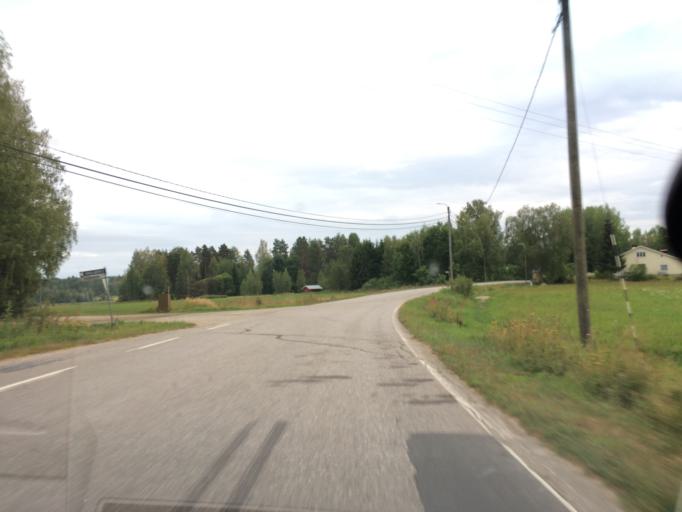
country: FI
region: Haeme
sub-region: Haemeenlinna
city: Tuulos
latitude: 61.1823
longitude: 24.7612
